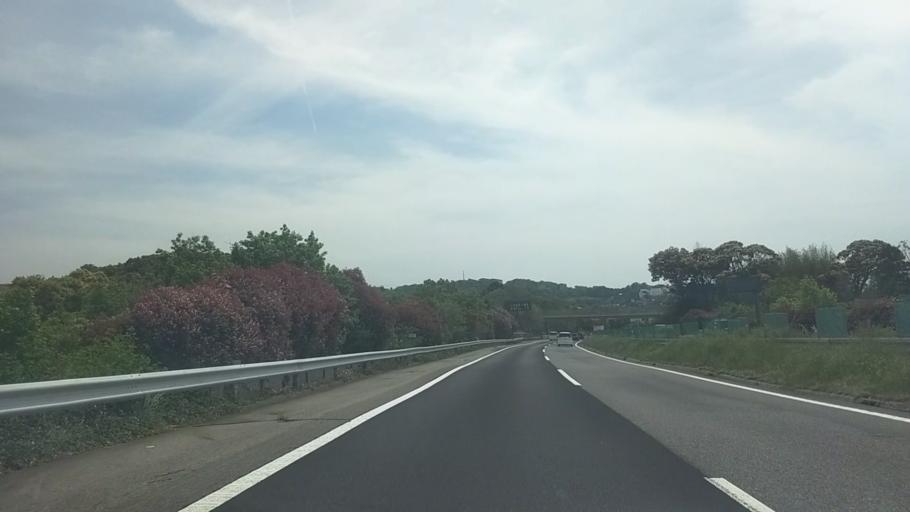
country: JP
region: Shizuoka
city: Kosai-shi
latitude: 34.8019
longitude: 137.5747
